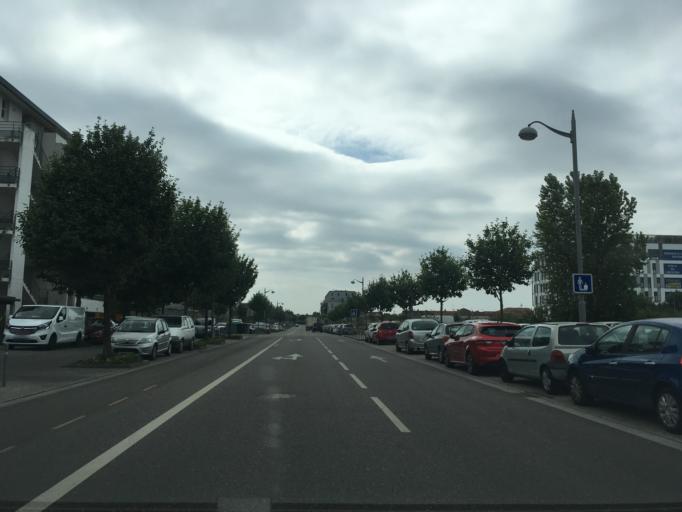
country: FR
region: Lorraine
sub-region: Departement de Meurthe-et-Moselle
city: Nancy
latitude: 48.6925
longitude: 6.1972
